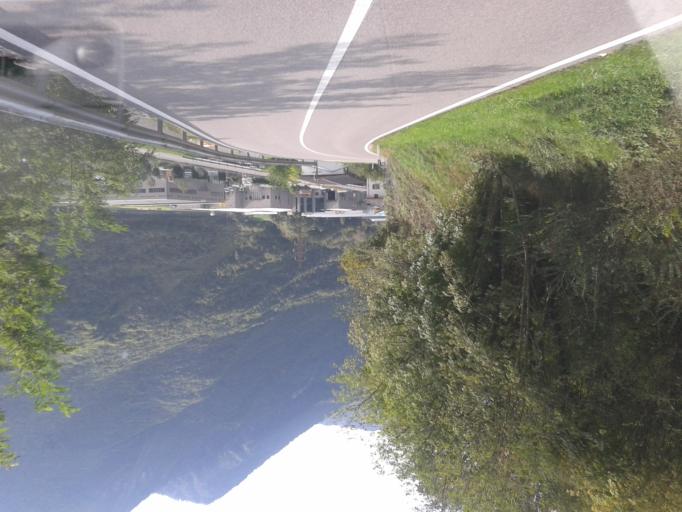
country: IT
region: Trentino-Alto Adige
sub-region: Provincia di Trento
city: Cimego
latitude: 45.9143
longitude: 10.6189
